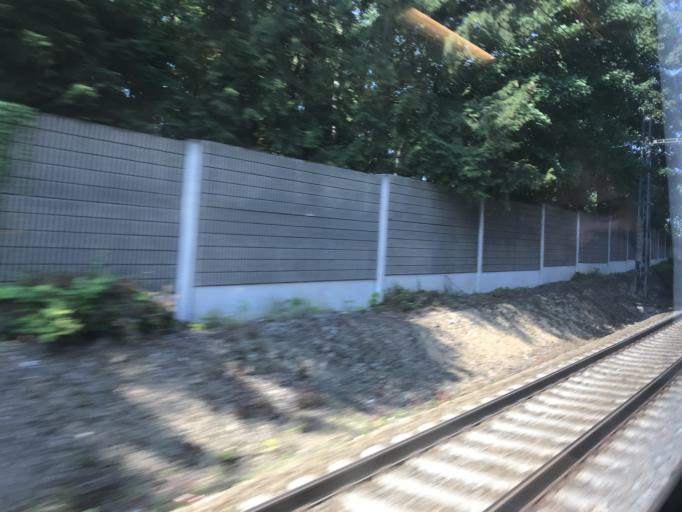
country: CZ
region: Central Bohemia
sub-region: Okres Praha-Vychod
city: Strancice
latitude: 49.9491
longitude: 14.6866
